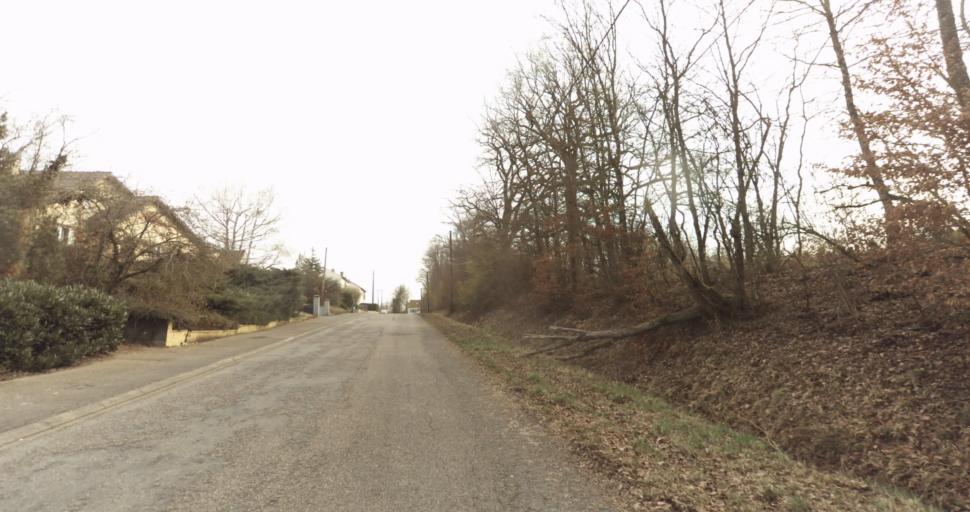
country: FR
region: Lorraine
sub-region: Departement de Meurthe-et-Moselle
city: Jarny
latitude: 49.1470
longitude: 5.8822
